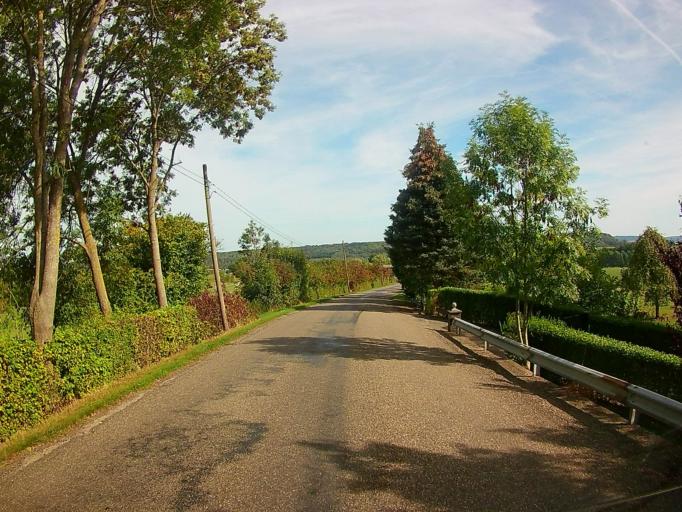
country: BE
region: Wallonia
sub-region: Province de Liege
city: Aubel
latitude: 50.7266
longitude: 5.8717
